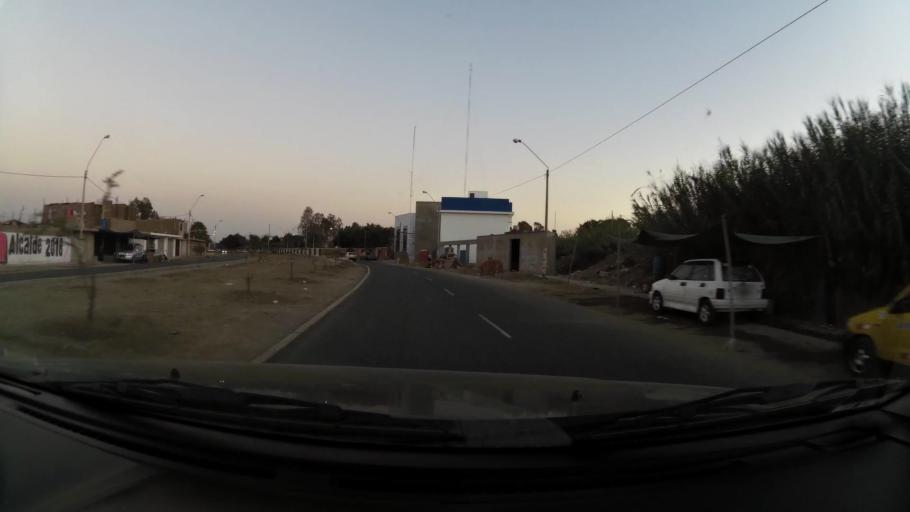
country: PE
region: Ica
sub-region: Provincia de Ica
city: Ica
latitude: -14.0733
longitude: -75.7354
